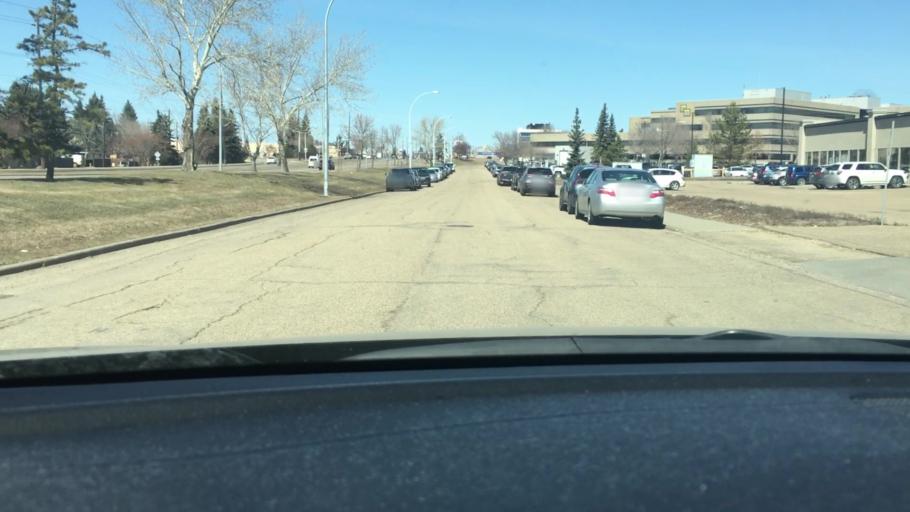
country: CA
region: Alberta
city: Edmonton
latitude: 53.5345
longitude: -113.4181
